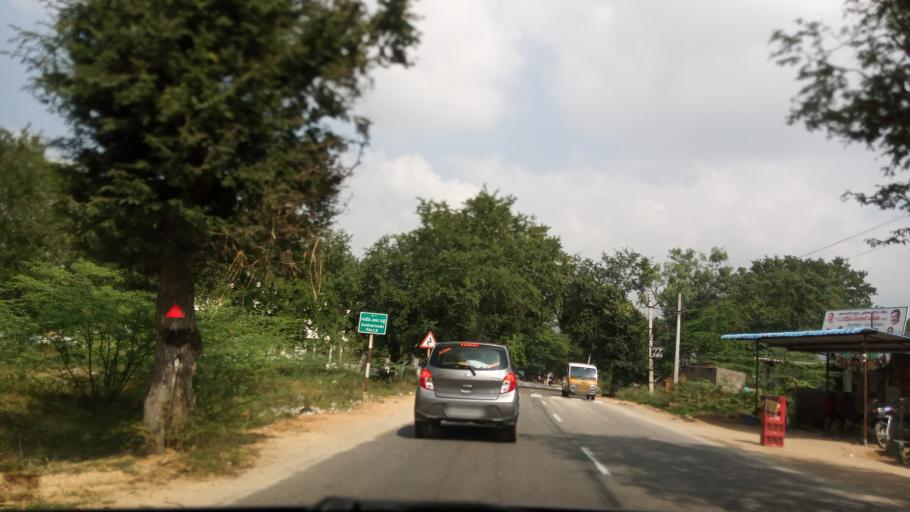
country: IN
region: Andhra Pradesh
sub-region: Chittoor
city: Madanapalle
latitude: 13.6296
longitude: 78.5519
